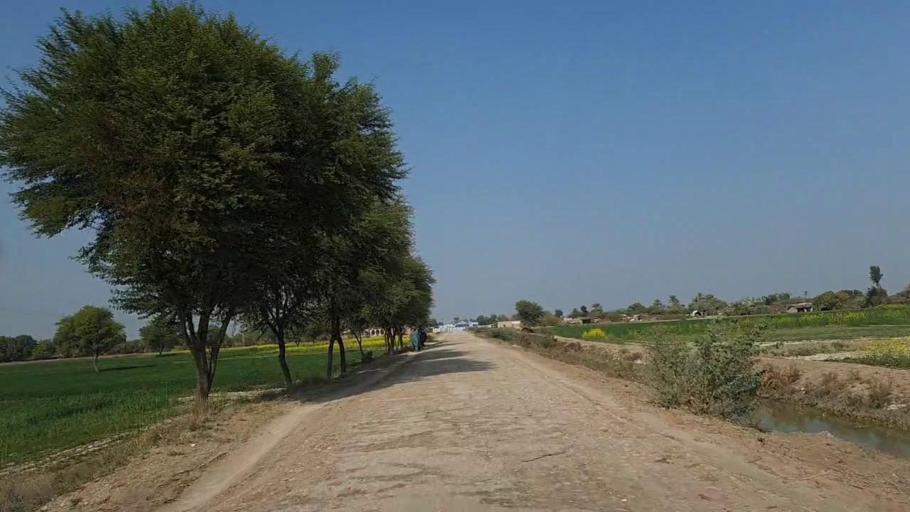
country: PK
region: Sindh
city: Jam Sahib
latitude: 26.2728
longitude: 68.5289
